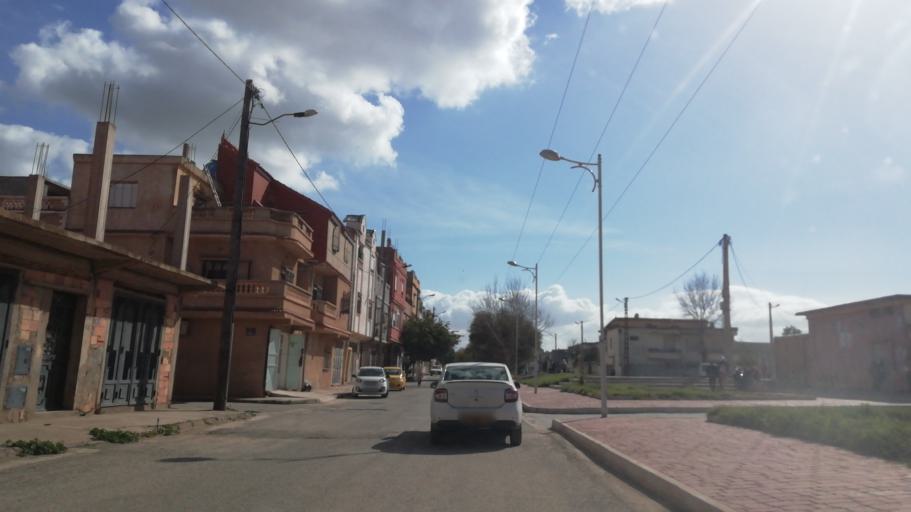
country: DZ
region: Oran
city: Es Senia
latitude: 35.6216
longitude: -0.5827
